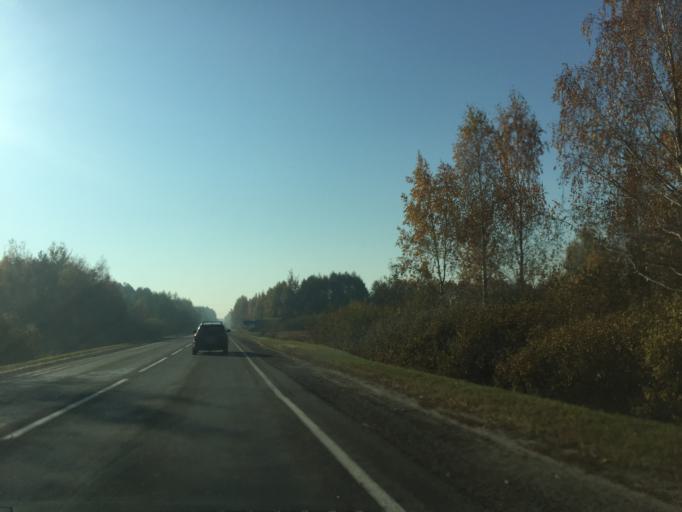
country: BY
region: Gomel
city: Kastsyukowka
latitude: 52.4403
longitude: 30.8256
